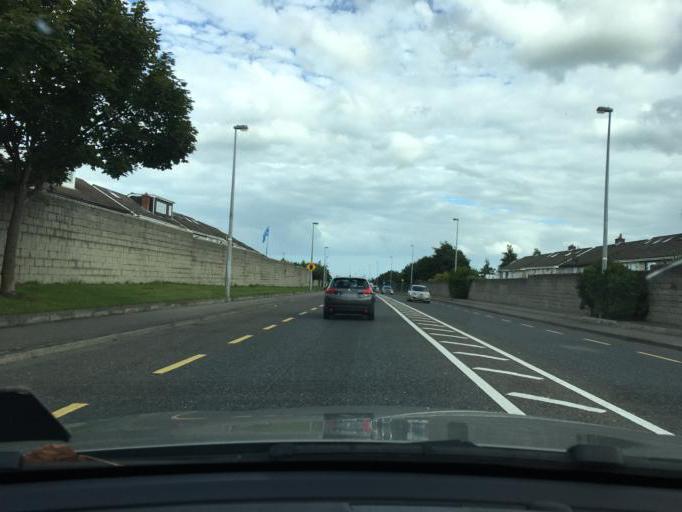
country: IE
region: Leinster
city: Donaghmede
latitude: 53.3984
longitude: -6.1585
